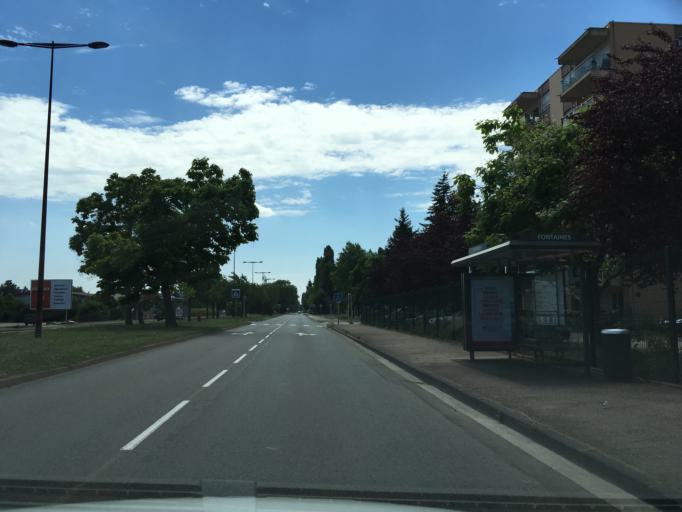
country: FR
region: Lorraine
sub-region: Departement de la Moselle
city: Woippy
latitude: 49.1466
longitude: 6.1716
